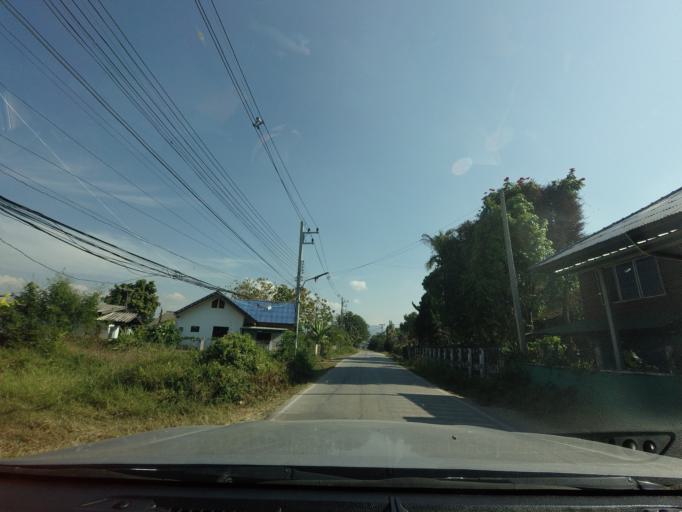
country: TH
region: Chiang Mai
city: San Kamphaeng
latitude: 18.7141
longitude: 99.1491
